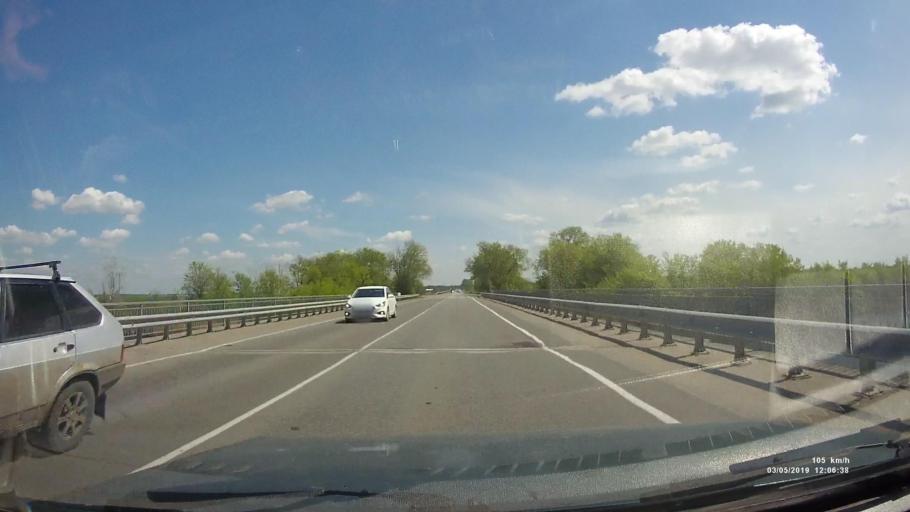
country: RU
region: Rostov
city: Bagayevskaya
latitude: 47.2854
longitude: 40.4561
